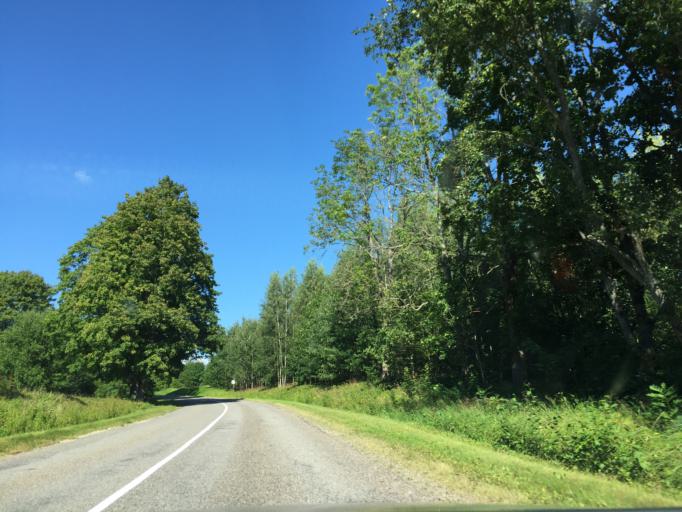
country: LV
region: Limbazu Rajons
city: Limbazi
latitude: 57.4764
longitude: 24.7112
